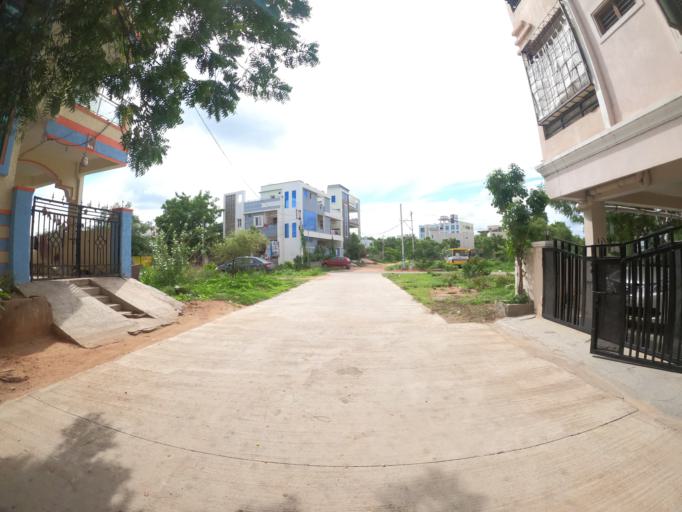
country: IN
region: Telangana
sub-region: Hyderabad
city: Hyderabad
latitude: 17.3527
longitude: 78.3883
